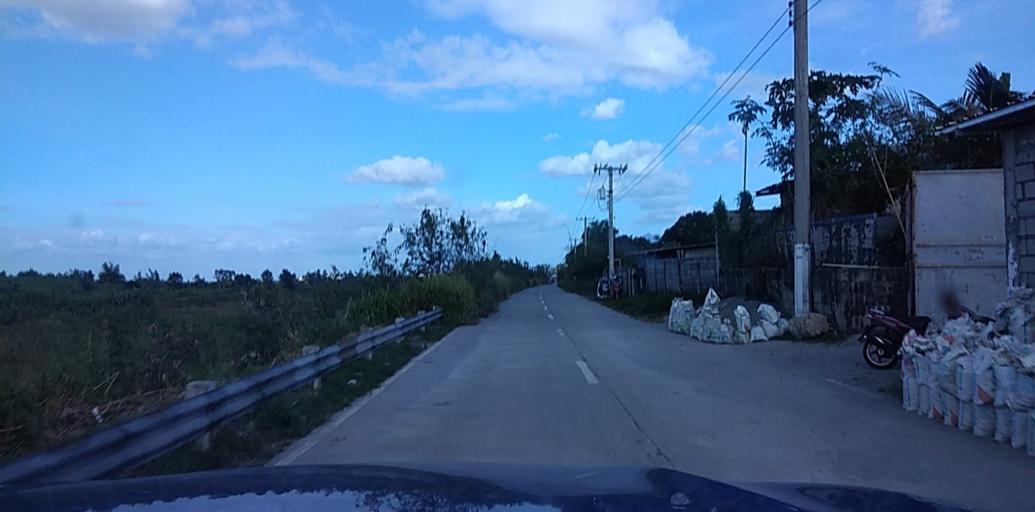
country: PH
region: Central Luzon
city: Santol
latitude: 15.1470
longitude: 120.5334
